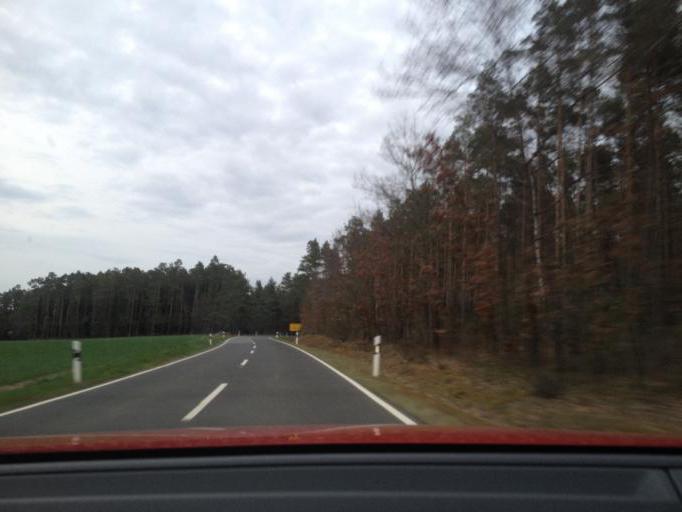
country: DE
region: Bavaria
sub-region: Upper Palatinate
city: Schlammersdorf
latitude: 49.7759
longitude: 11.7719
